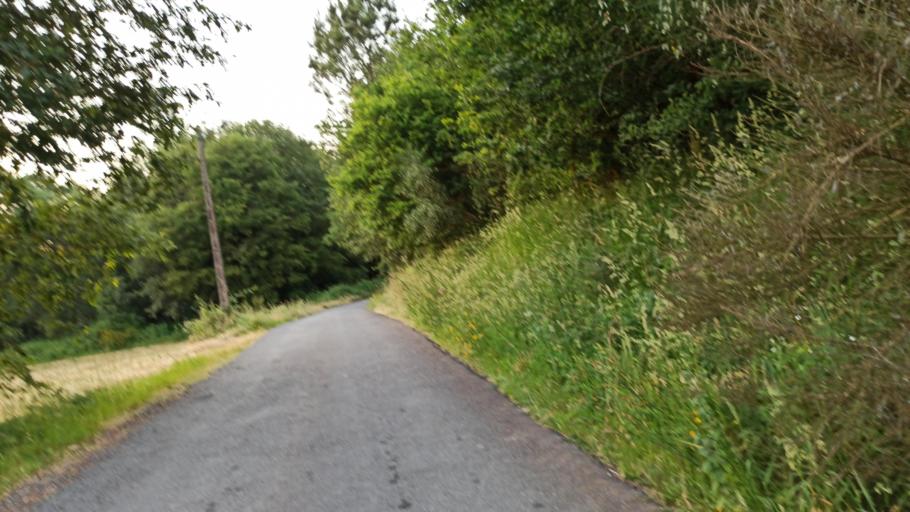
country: ES
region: Galicia
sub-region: Provincia da Coruna
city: Negreira
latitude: 42.9179
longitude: -8.7498
